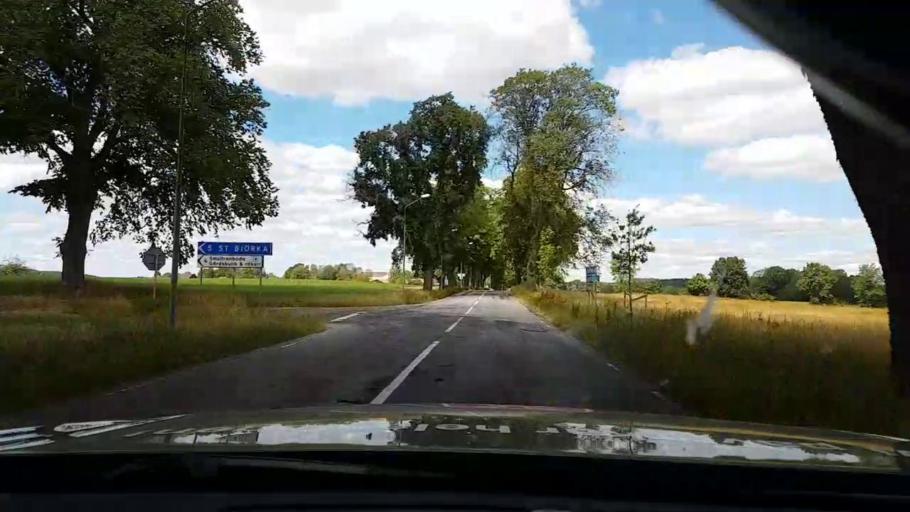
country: SE
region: Kalmar
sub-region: Vasterviks Kommun
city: Forserum
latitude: 58.0076
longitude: 16.4839
